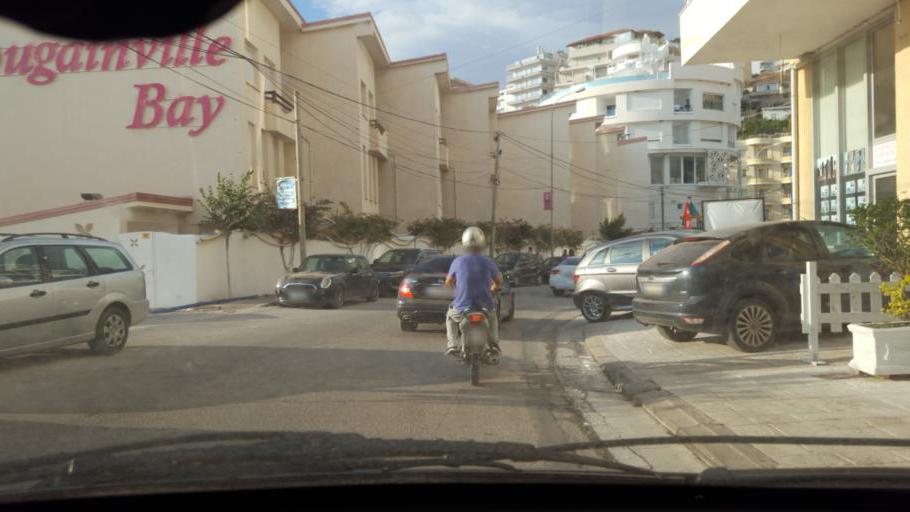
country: AL
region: Vlore
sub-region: Rrethi i Sarandes
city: Sarande
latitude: 39.8627
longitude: 20.0187
